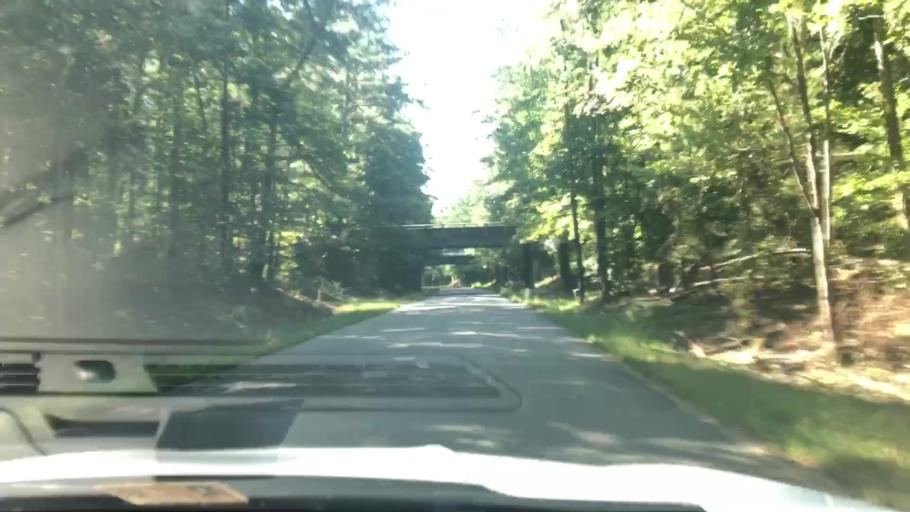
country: US
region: Virginia
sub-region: New Kent County
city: New Kent
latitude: 37.4848
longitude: -76.9350
